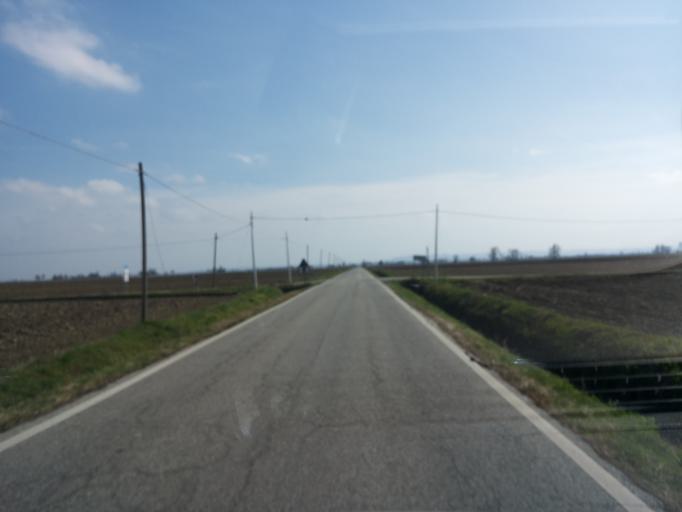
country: IT
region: Piedmont
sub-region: Provincia di Vercelli
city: Crova
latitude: 45.3169
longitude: 8.1978
